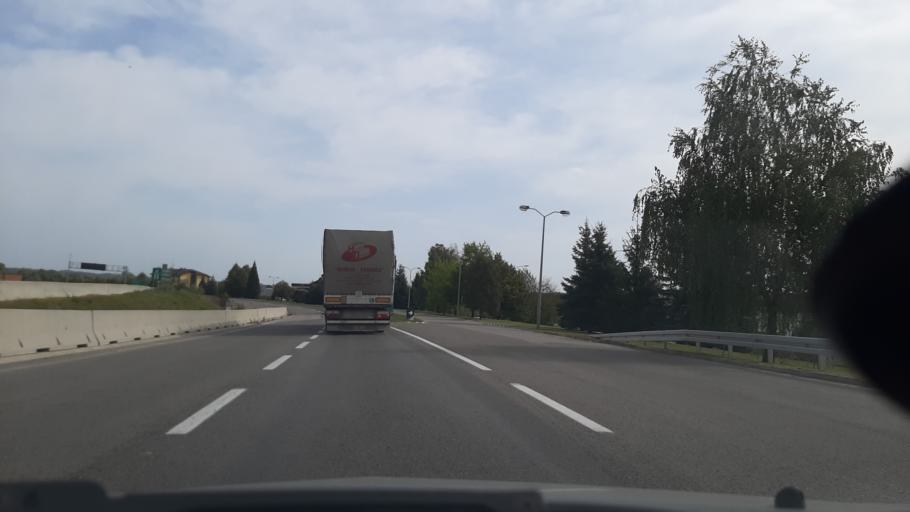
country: BA
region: Republika Srpska
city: Trn
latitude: 44.8703
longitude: 17.2725
